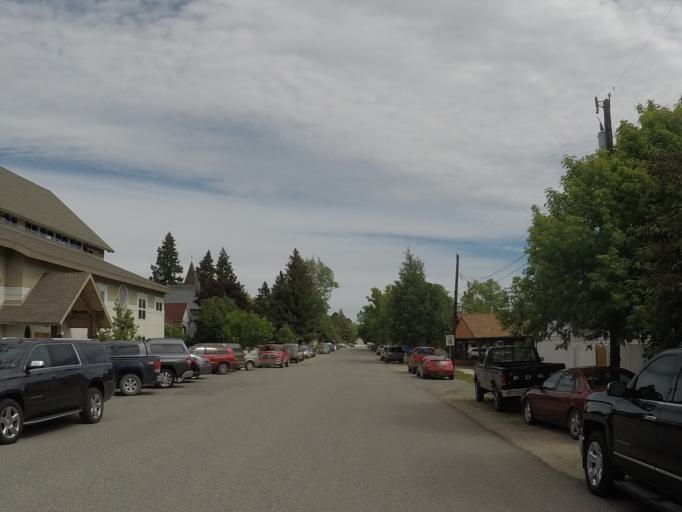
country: US
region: Montana
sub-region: Carbon County
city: Red Lodge
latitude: 45.1870
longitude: -109.2498
